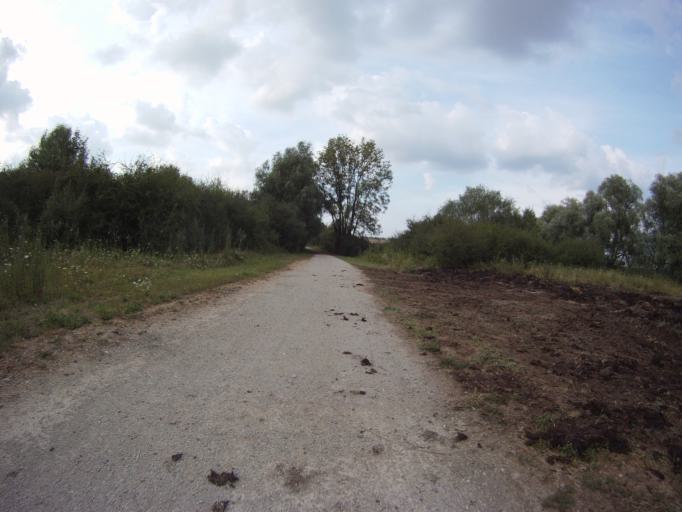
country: FR
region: Lorraine
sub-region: Departement de la Moselle
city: Mecleuves
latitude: 49.0663
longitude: 6.3144
